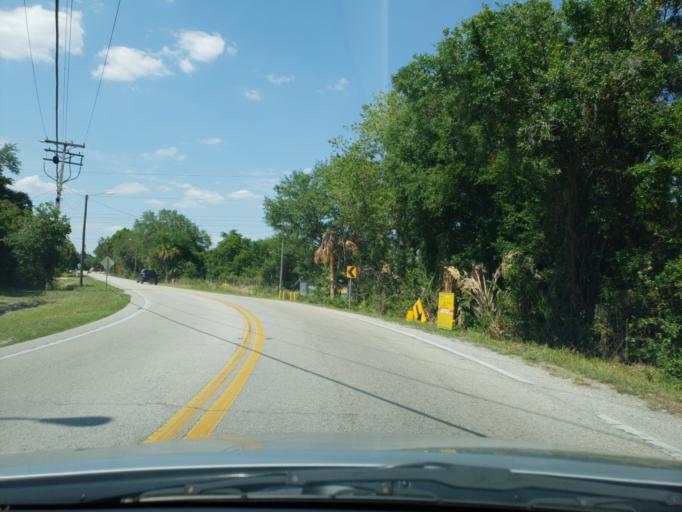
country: US
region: Florida
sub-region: Hillsborough County
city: Riverview
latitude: 27.8685
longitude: -82.3391
